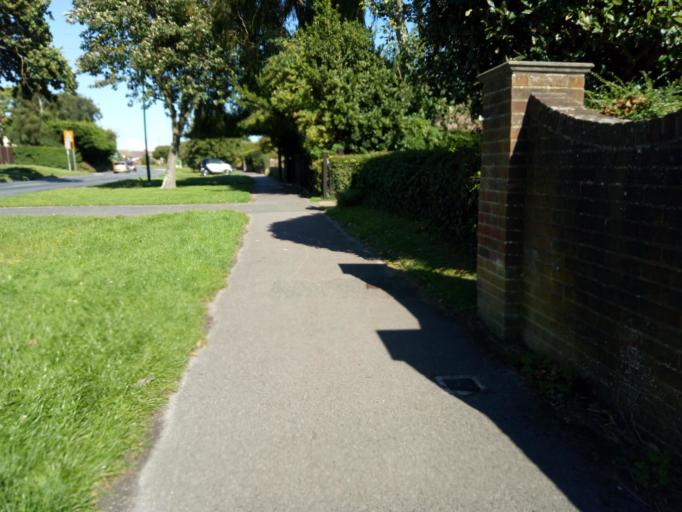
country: GB
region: England
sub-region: West Sussex
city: Barnham
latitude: 50.7942
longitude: -0.6357
